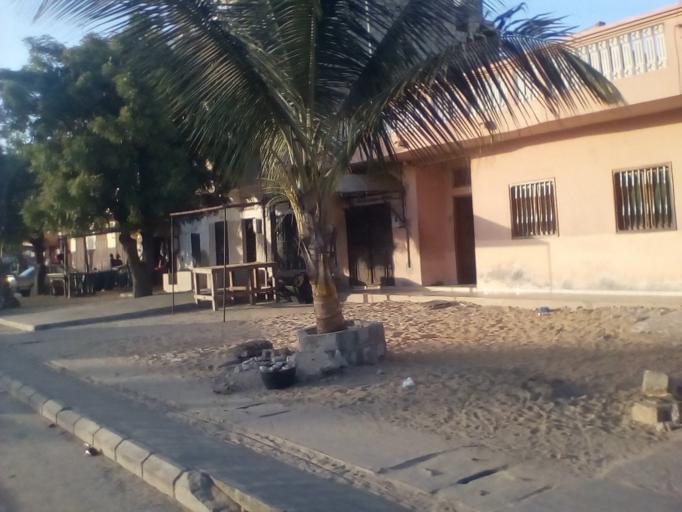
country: SN
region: Saint-Louis
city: Saint-Louis
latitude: 16.0187
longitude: -16.4935
